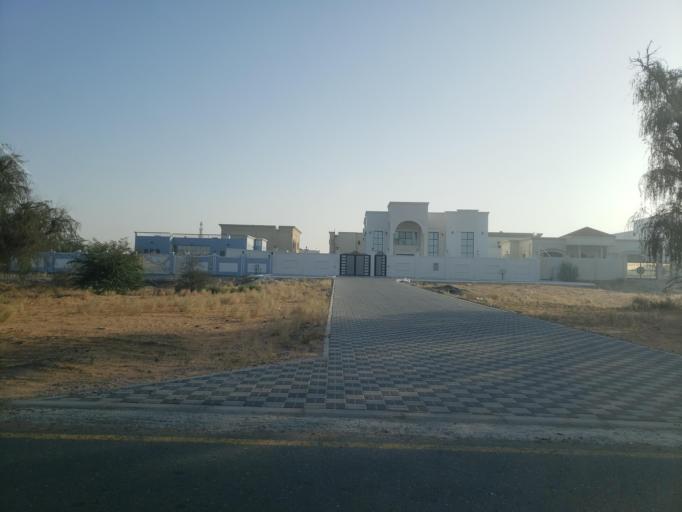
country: AE
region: Umm al Qaywayn
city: Umm al Qaywayn
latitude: 25.4721
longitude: 55.6105
